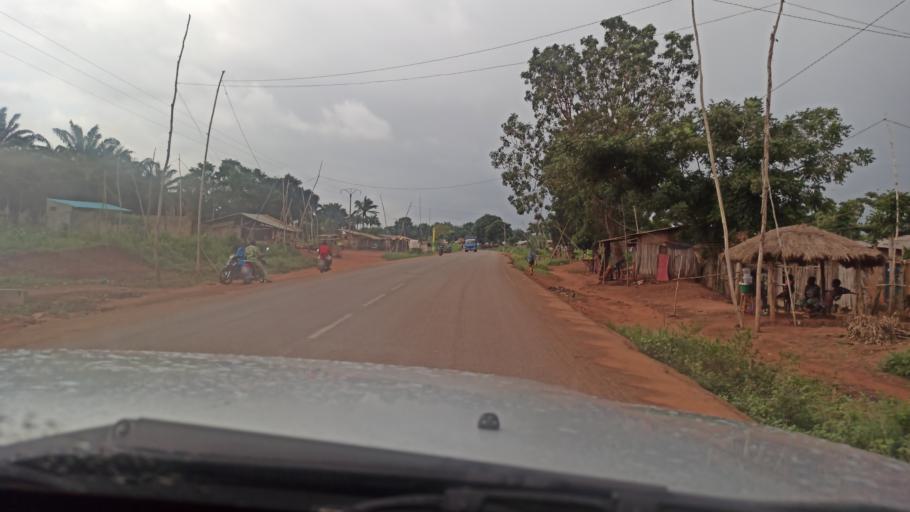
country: BJ
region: Queme
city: Porto-Novo
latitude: 6.5629
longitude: 2.5821
